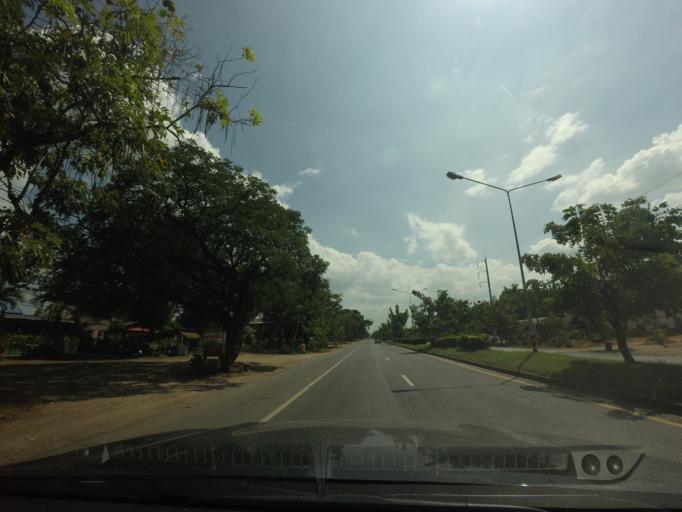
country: TH
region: Phetchabun
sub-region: Amphoe Bueng Sam Phan
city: Bueng Sam Phan
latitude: 15.8562
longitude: 101.0115
